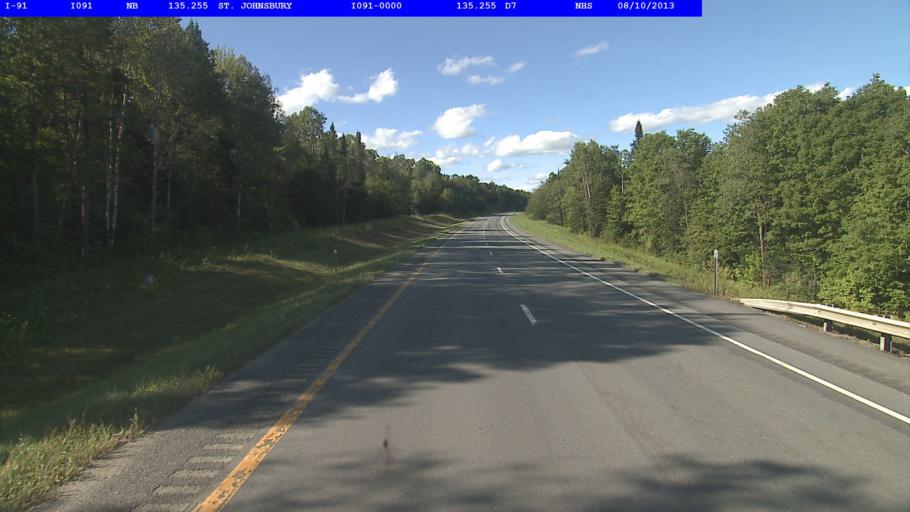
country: US
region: Vermont
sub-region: Caledonia County
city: Lyndon
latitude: 44.4925
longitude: -72.0214
